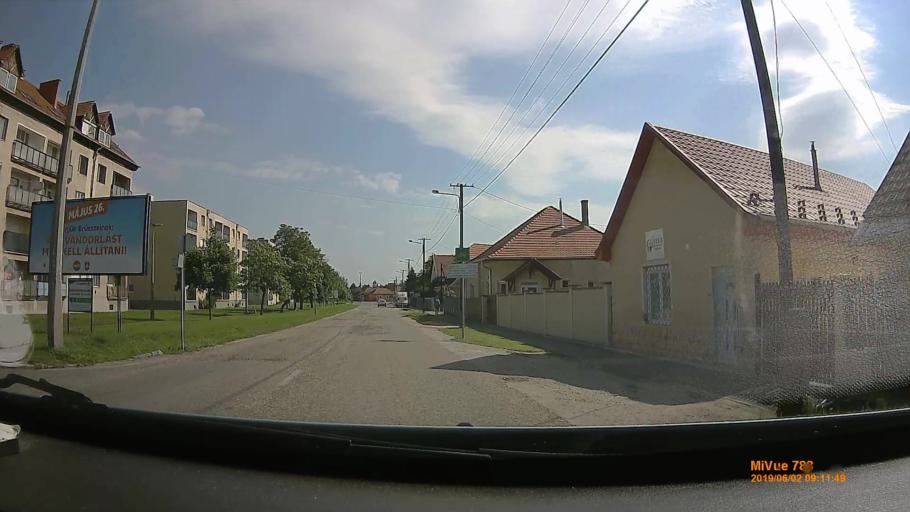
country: HU
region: Borsod-Abauj-Zemplen
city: Sajoszentpeter
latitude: 48.2183
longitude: 20.7040
